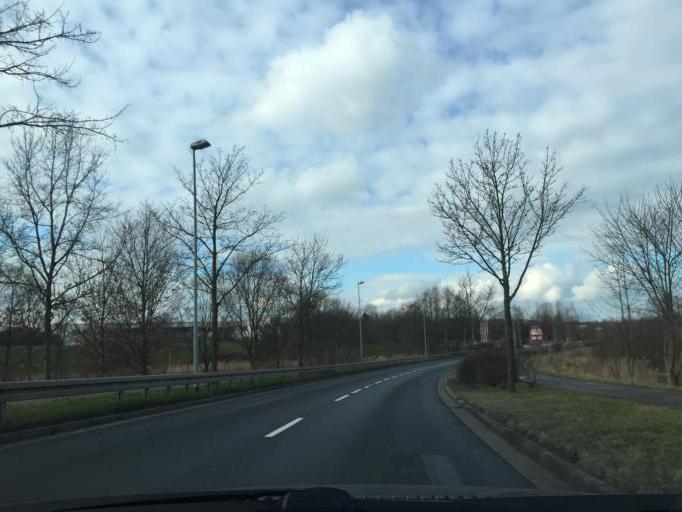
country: DE
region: Saxony
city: Radeberg
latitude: 51.1253
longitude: 13.9281
